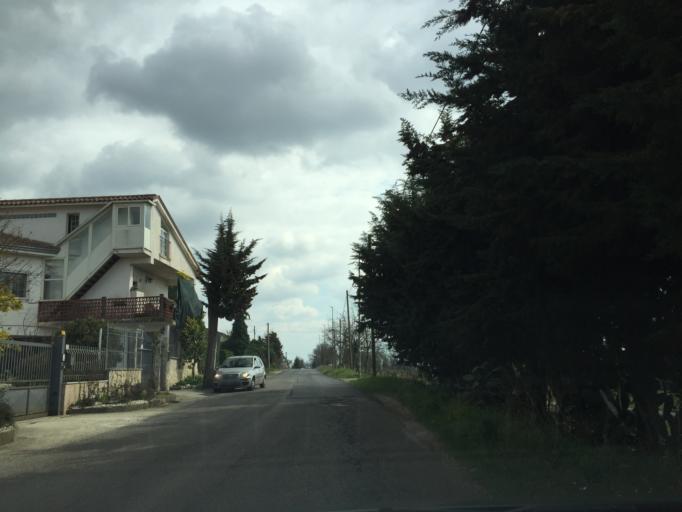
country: IT
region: Latium
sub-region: Provincia di Frosinone
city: Piedimonte San Germano Alta
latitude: 41.5019
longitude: 13.7365
